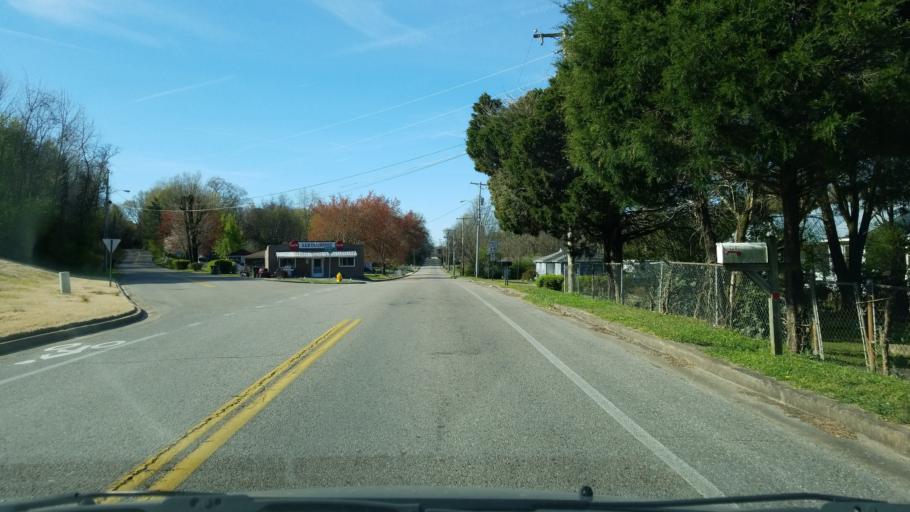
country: US
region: Tennessee
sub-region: Hamilton County
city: East Brainerd
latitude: 35.0495
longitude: -85.1815
